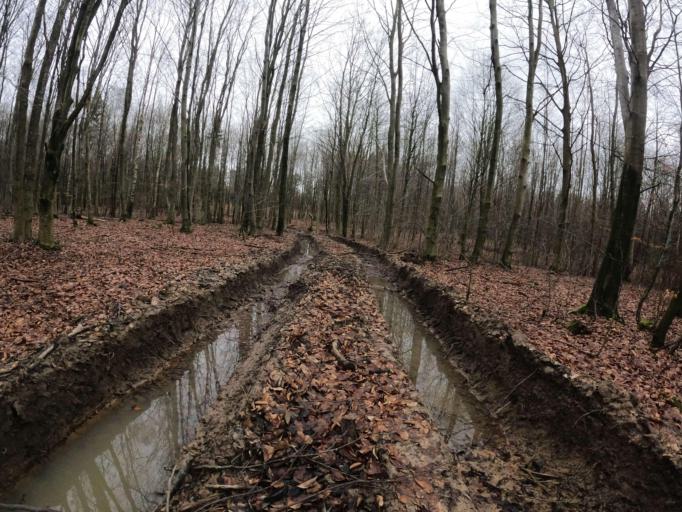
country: PL
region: West Pomeranian Voivodeship
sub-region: Powiat slawienski
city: Darlowo
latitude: 54.3924
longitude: 16.4998
